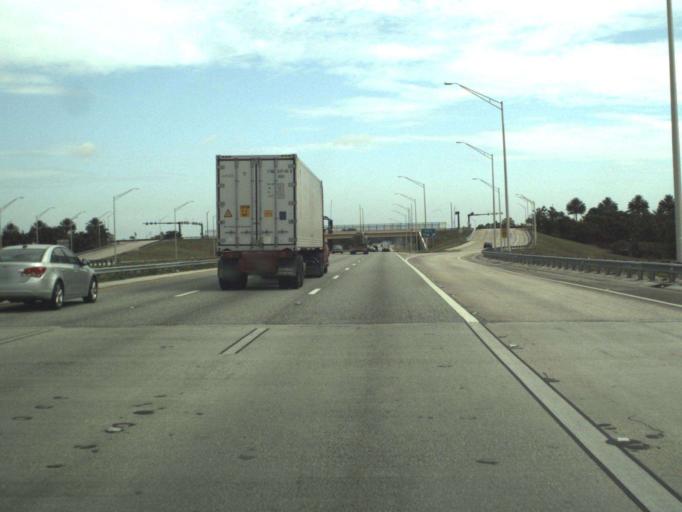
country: US
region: Florida
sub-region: Saint Lucie County
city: Port Saint Lucie
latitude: 27.2061
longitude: -80.4003
